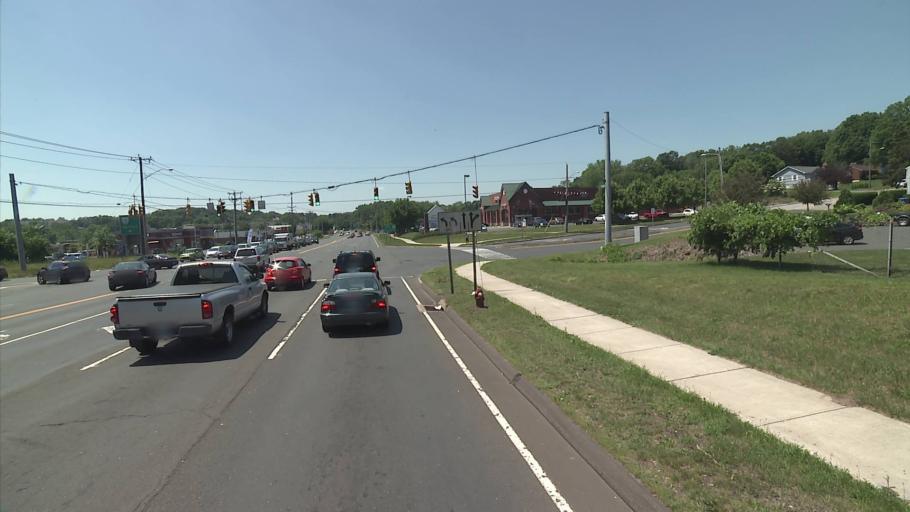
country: US
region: Connecticut
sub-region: Hartford County
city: Manchester
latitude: 41.8129
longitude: -72.5241
